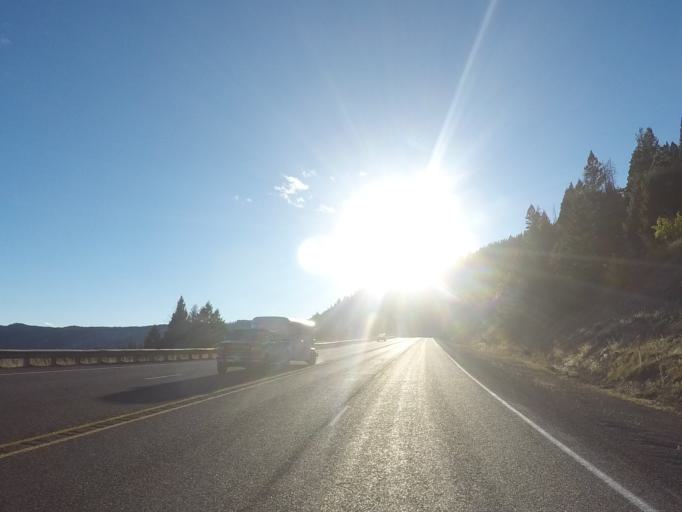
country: US
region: Montana
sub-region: Lewis and Clark County
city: Helena West Side
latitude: 46.5824
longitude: -112.2701
